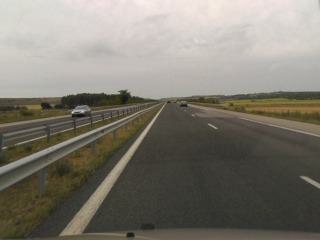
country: BG
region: Stara Zagora
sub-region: Obshtina Chirpan
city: Chirpan
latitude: 42.2152
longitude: 25.3209
